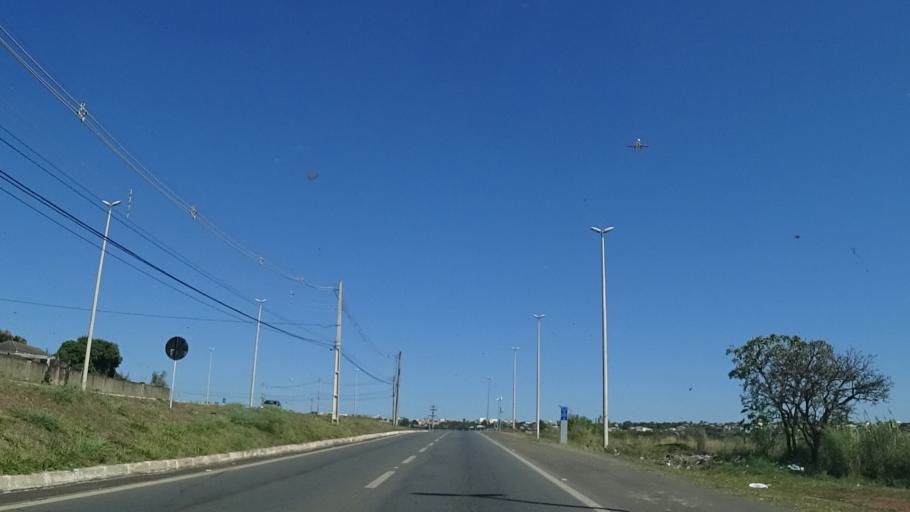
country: BR
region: Federal District
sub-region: Brasilia
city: Brasilia
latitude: -15.8678
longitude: -47.9900
